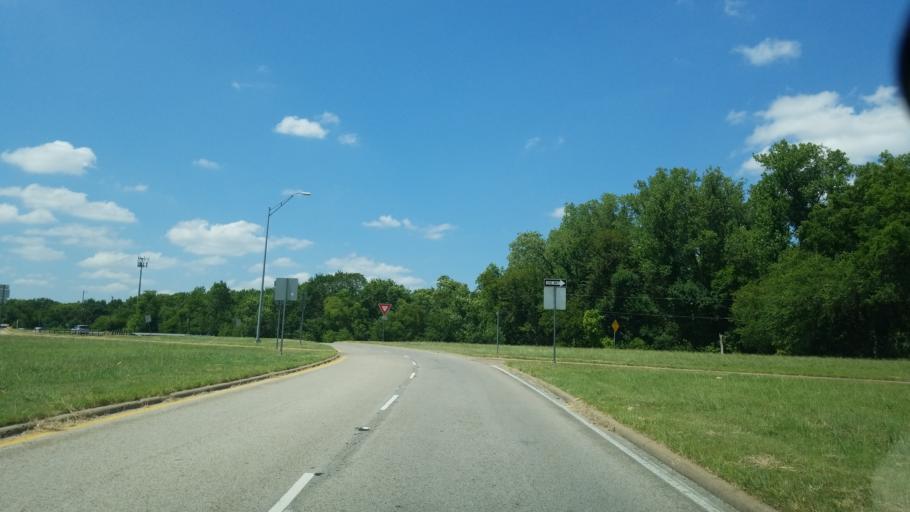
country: US
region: Texas
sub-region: Dallas County
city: Dallas
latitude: 32.7456
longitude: -96.7272
